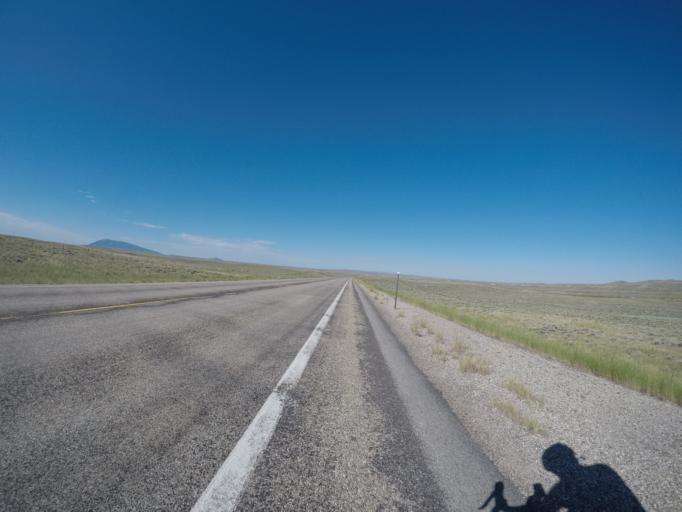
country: US
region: Wyoming
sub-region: Carbon County
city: Saratoga
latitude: 41.8802
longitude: -106.4850
